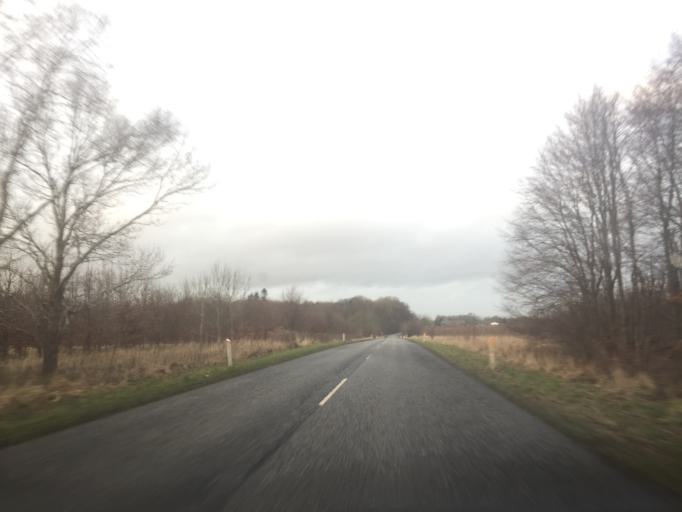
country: DK
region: Capital Region
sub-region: Egedal Kommune
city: Smorumnedre
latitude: 55.6955
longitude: 12.3229
